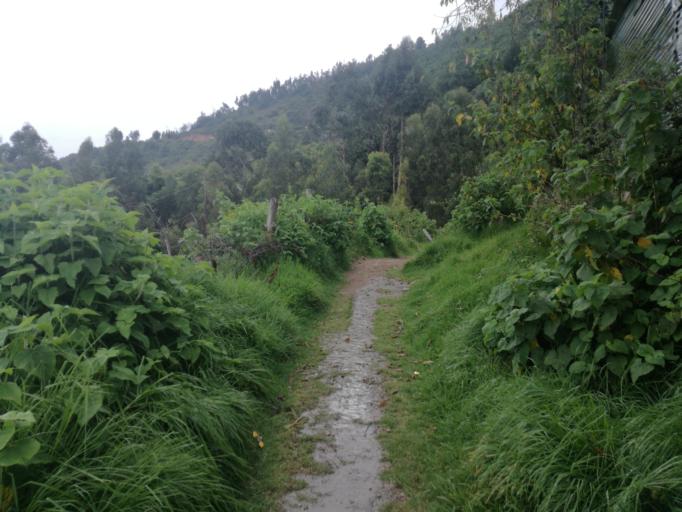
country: CO
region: Boyaca
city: Socha Viejo
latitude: 5.9988
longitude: -72.6877
